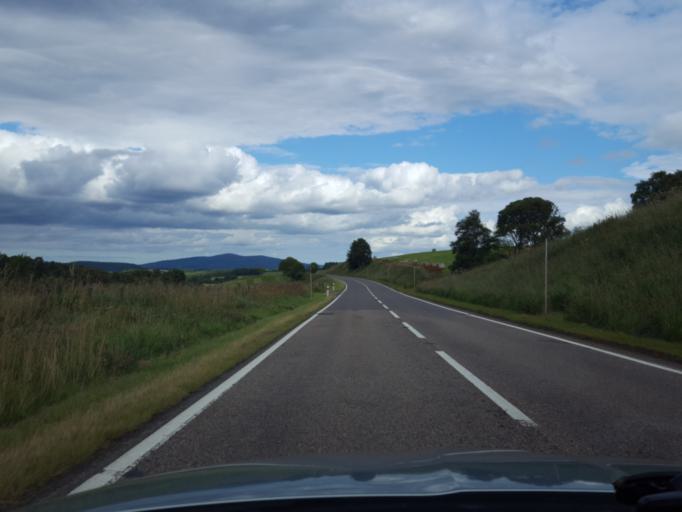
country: GB
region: Scotland
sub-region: Moray
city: Rothes
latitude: 57.4399
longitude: -3.2900
